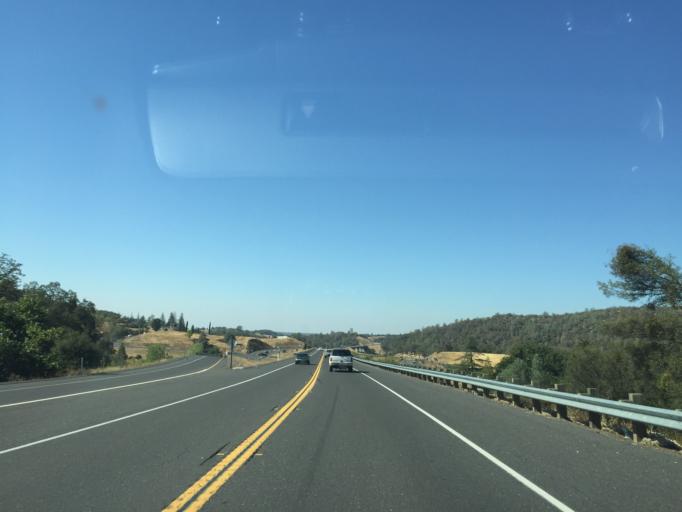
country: US
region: California
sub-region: Tuolumne County
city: East Sonora
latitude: 37.9811
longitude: -120.3319
